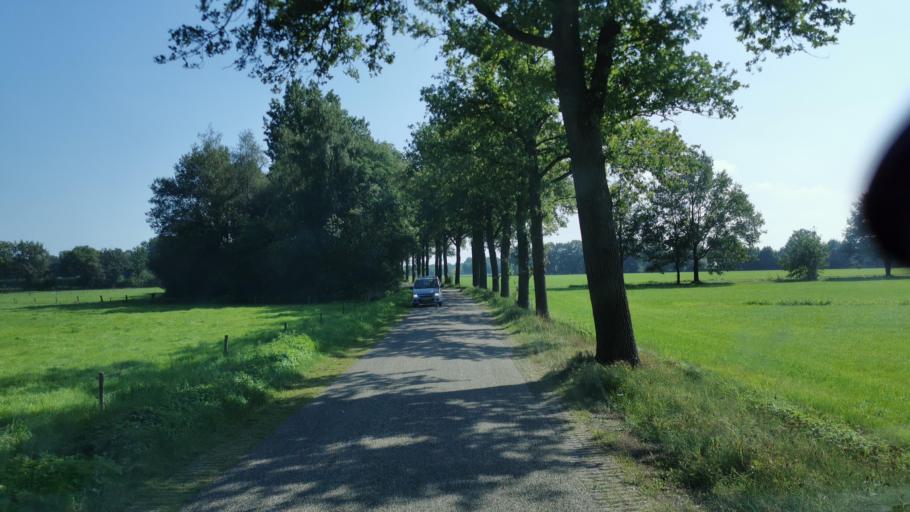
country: NL
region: Overijssel
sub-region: Gemeente Oldenzaal
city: Oldenzaal
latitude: 52.3311
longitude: 6.8856
